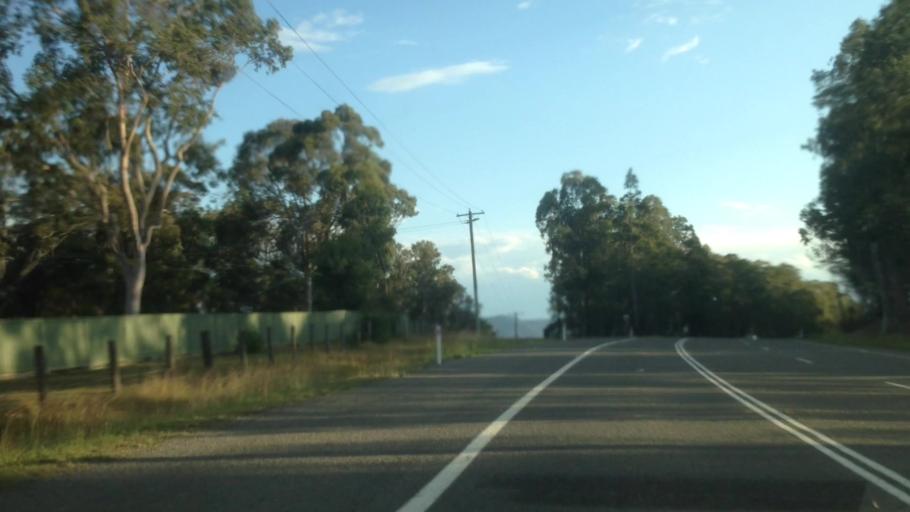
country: AU
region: New South Wales
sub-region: Cessnock
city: Kurri Kurri
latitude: -32.8598
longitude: 151.4840
